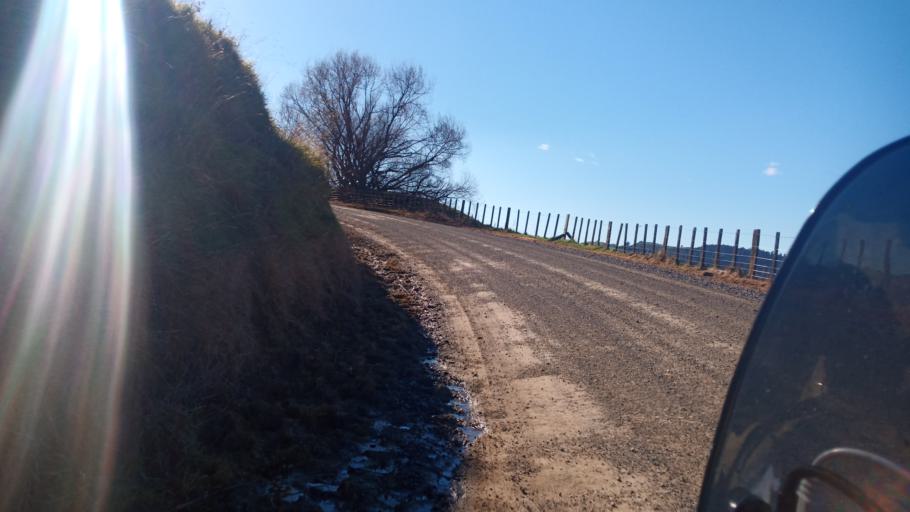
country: NZ
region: Hawke's Bay
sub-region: Wairoa District
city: Wairoa
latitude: -38.7759
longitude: 177.2654
